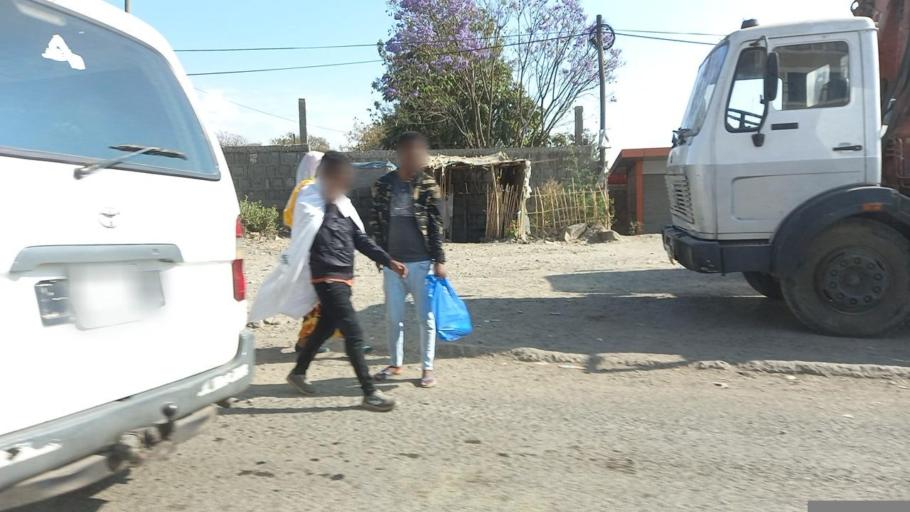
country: ET
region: Adis Abeba
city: Addis Ababa
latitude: 8.9381
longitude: 38.7631
